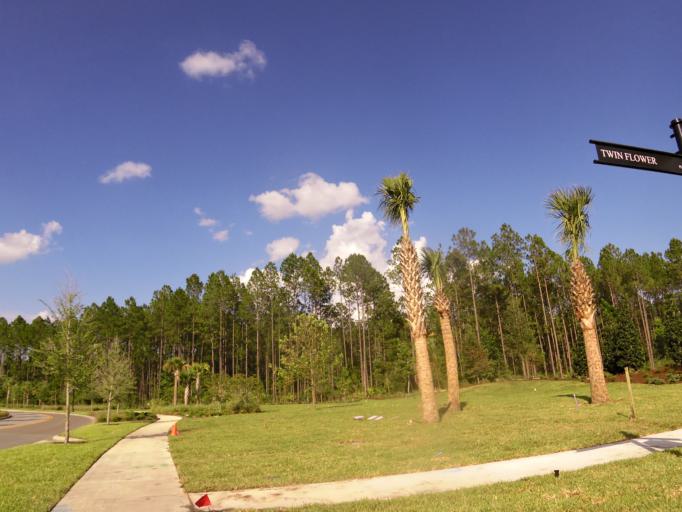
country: US
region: Florida
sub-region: Clay County
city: Green Cove Springs
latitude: 30.0343
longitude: -81.6242
